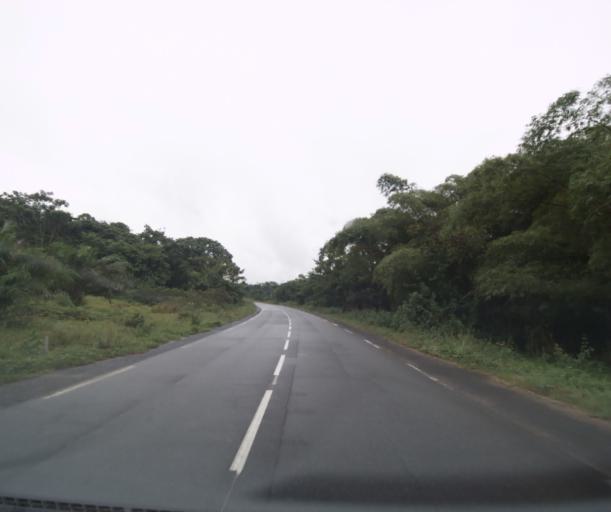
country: CM
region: Littoral
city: Dizangue
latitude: 3.3825
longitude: 10.1041
